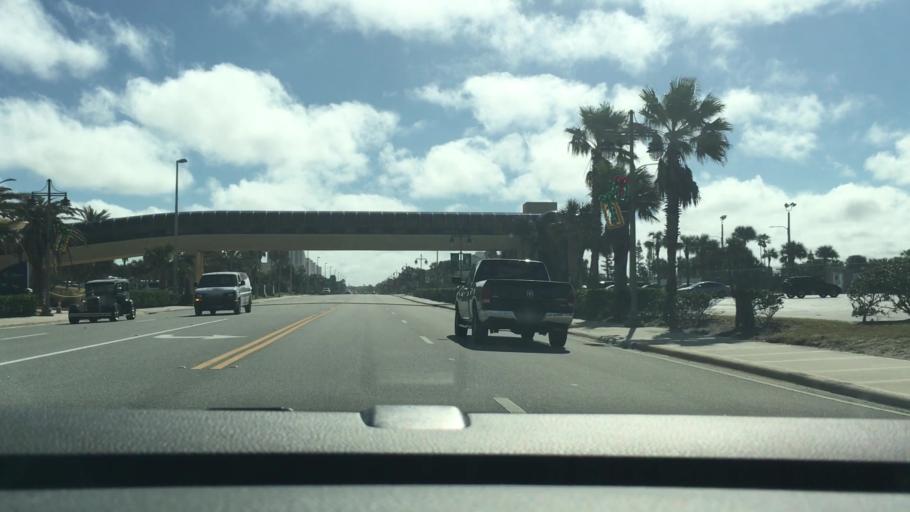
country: US
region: Florida
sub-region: Volusia County
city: Daytona Beach Shores
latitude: 29.1815
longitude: -80.9857
